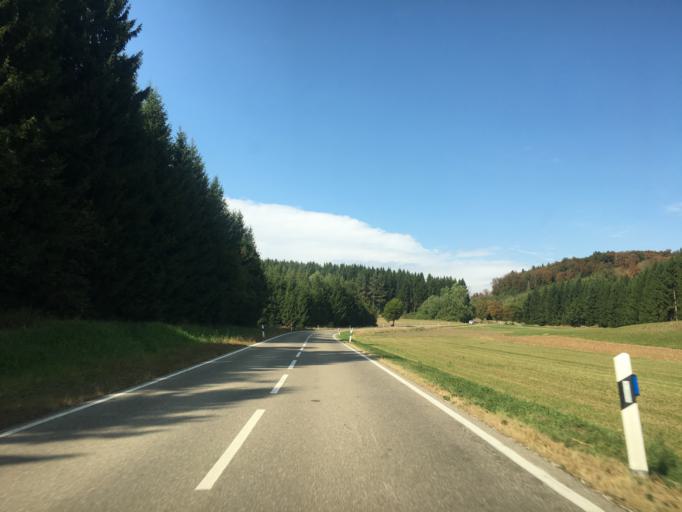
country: DE
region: Baden-Wuerttemberg
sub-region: Tuebingen Region
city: Trochtelfingen
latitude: 48.3712
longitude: 9.1990
